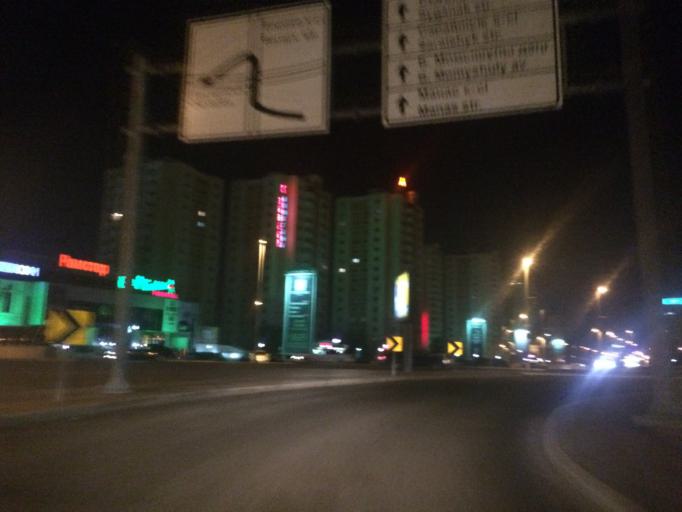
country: KZ
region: Astana Qalasy
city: Astana
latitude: 51.1534
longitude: 71.4312
